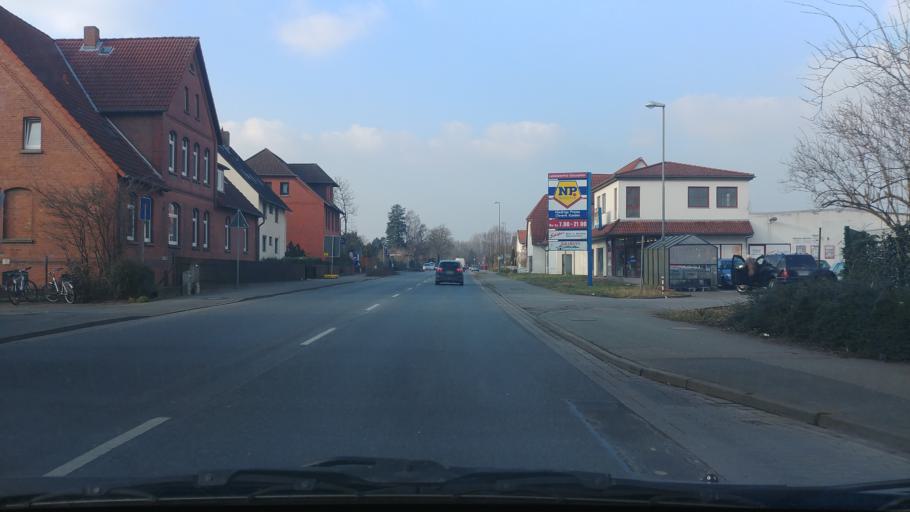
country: DE
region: Lower Saxony
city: Hemmingen
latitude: 52.3047
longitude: 9.7378
